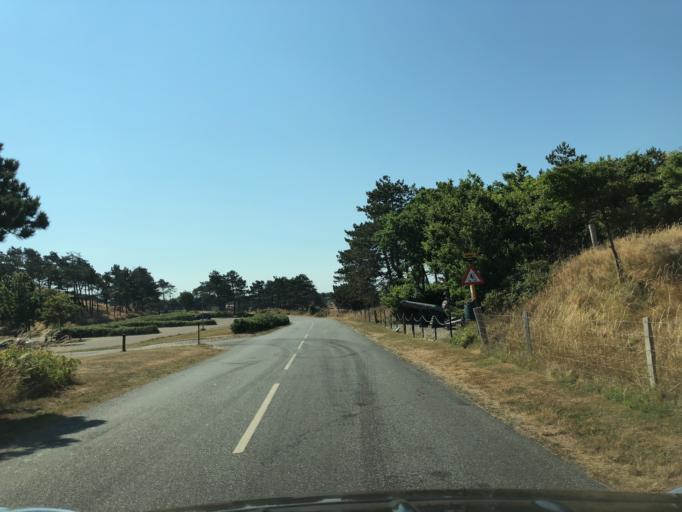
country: DK
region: Zealand
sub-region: Odsherred Kommune
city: Asnaes
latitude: 56.0066
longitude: 11.2794
